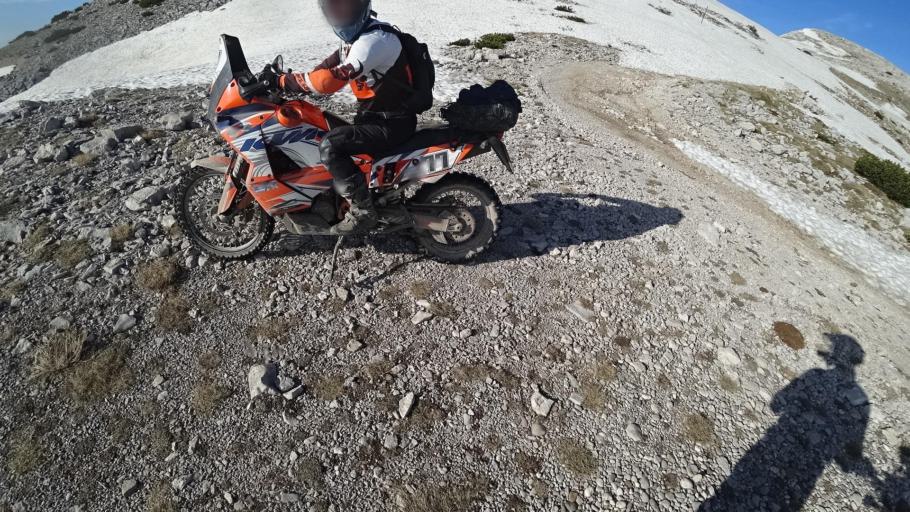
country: BA
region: Federation of Bosnia and Herzegovina
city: Kocerin
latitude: 43.6013
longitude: 17.5468
